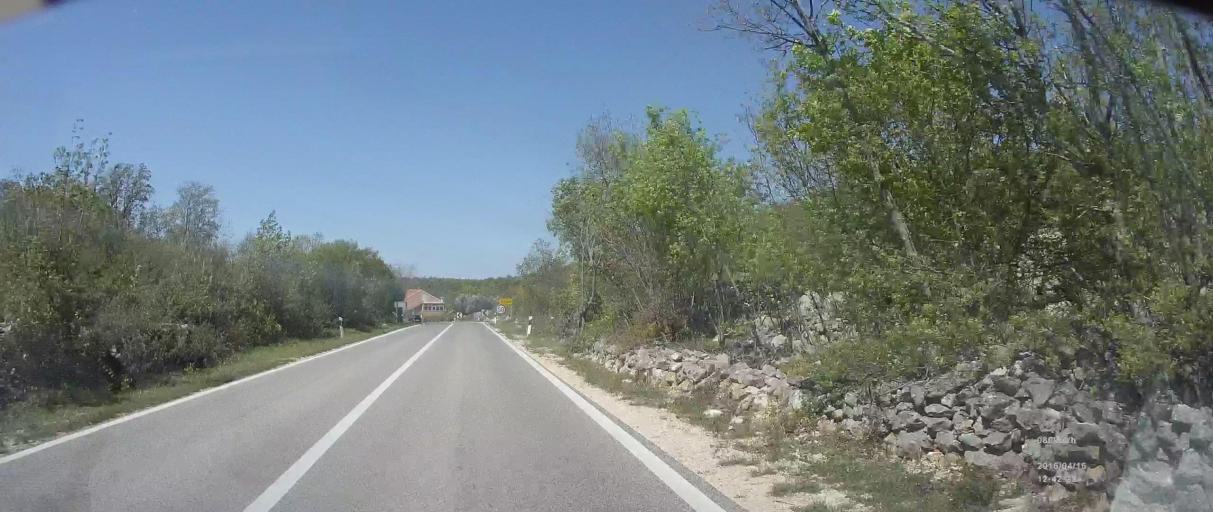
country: HR
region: Sibensko-Kniniska
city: Rogoznica
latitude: 43.6288
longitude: 16.0904
